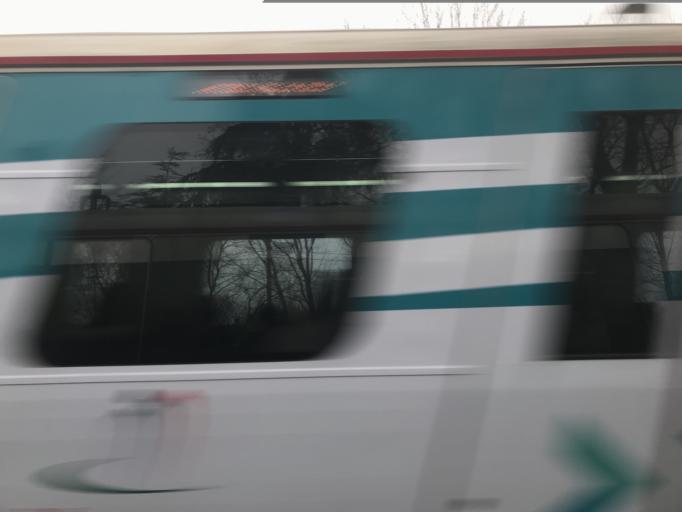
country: TR
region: Kocaeli
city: Darica
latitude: 40.8097
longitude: 29.3528
